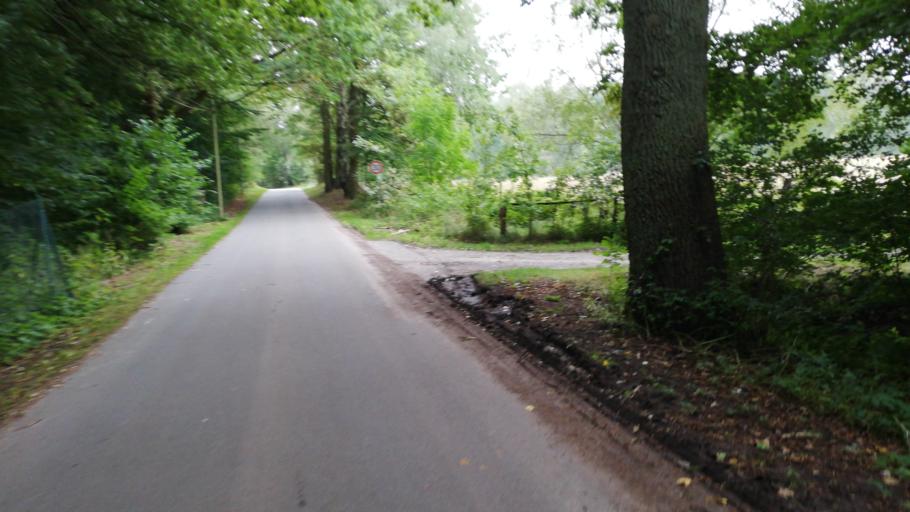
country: DE
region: Brandenburg
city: Rheinsberg
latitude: 53.1012
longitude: 12.8479
